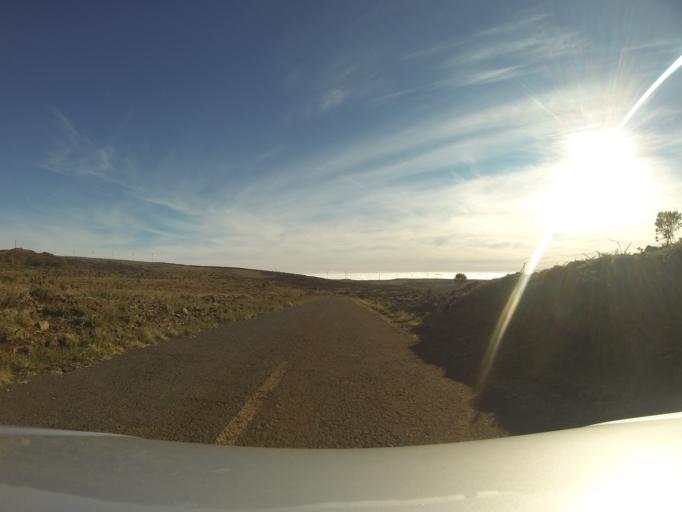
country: PT
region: Madeira
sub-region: Sao Vicente
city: Sao Vicente
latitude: 32.7653
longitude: -17.0815
